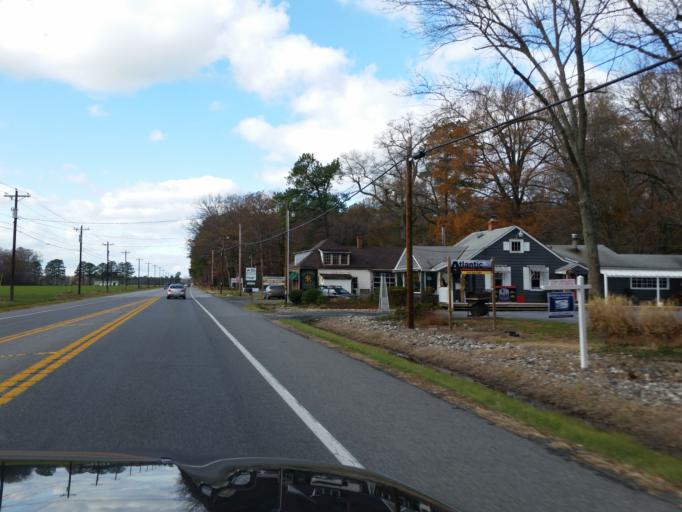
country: US
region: Maryland
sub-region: Talbot County
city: Easton
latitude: 38.7799
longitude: -76.0950
